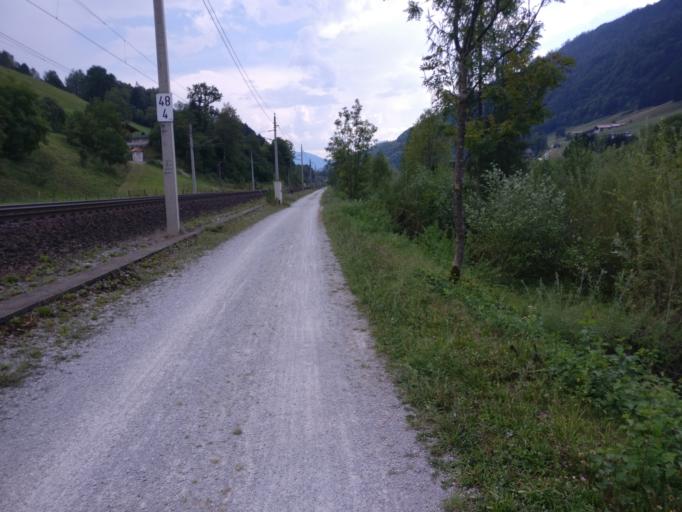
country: AT
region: Salzburg
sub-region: Politischer Bezirk Sankt Johann im Pongau
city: Pfarrwerfen
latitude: 47.4496
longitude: 13.2135
